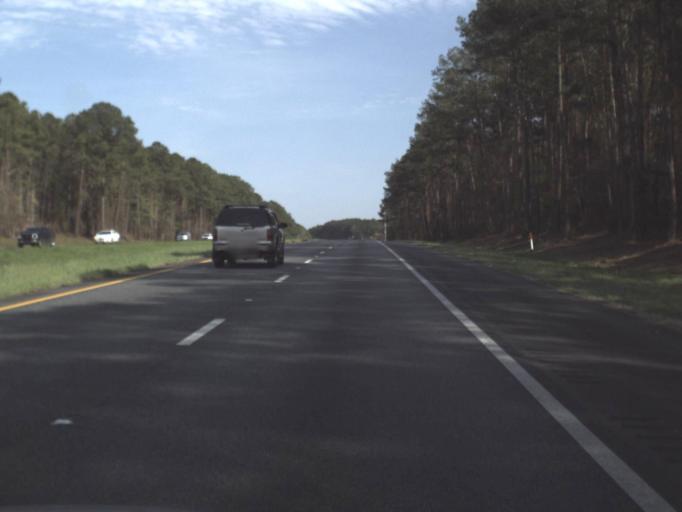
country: US
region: Florida
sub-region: Leon County
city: Tallahassee
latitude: 30.4994
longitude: -84.2174
